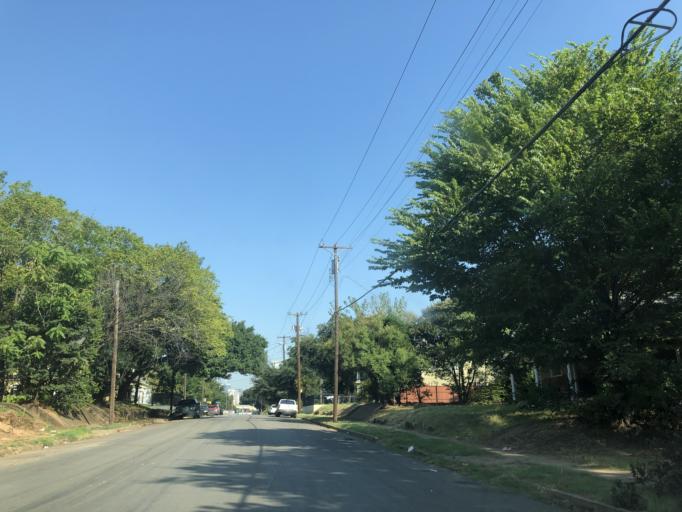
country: US
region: Texas
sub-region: Dallas County
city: Dallas
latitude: 32.7555
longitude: -96.7694
